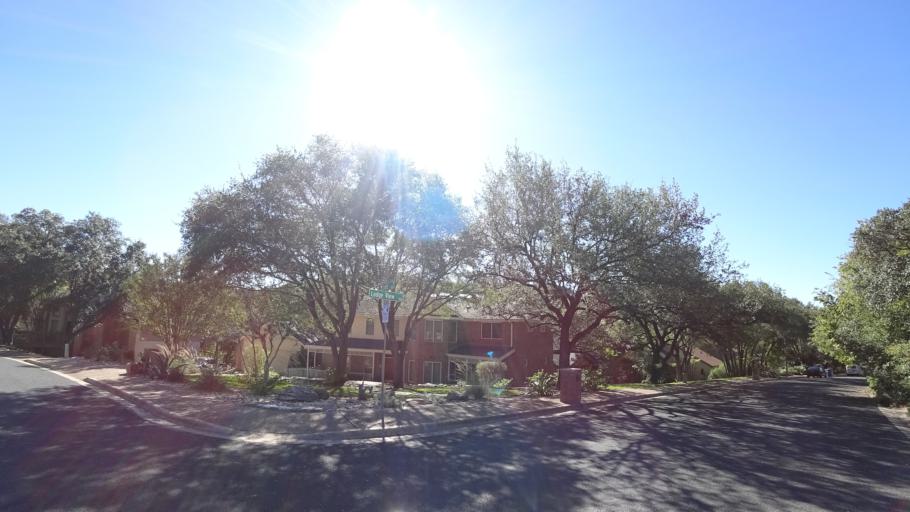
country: US
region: Texas
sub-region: Travis County
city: West Lake Hills
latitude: 30.3593
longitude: -97.7830
